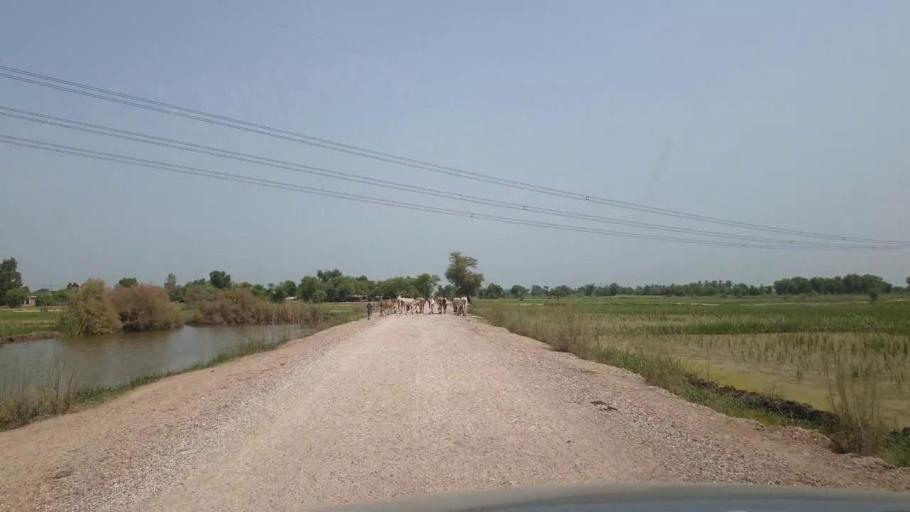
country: PK
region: Sindh
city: Madeji
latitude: 27.8056
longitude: 68.5203
